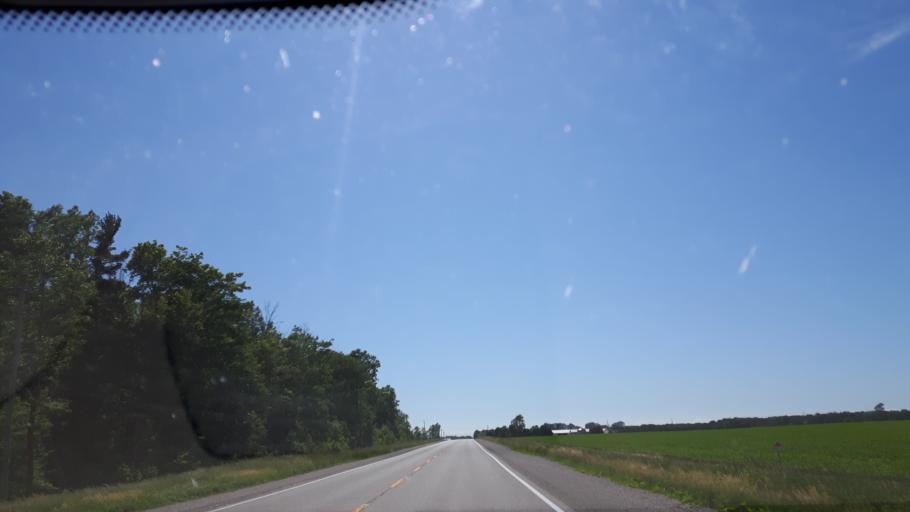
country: CA
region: Ontario
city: Bluewater
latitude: 43.4274
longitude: -81.5654
